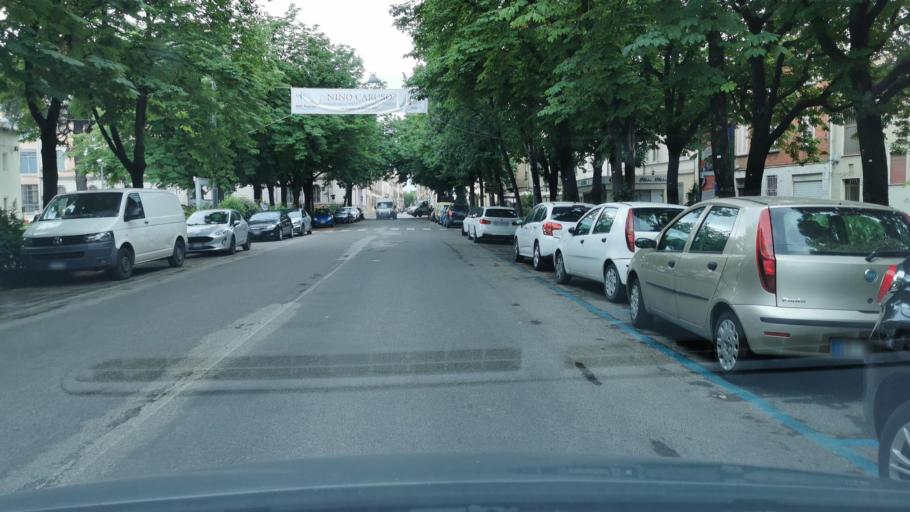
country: IT
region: Emilia-Romagna
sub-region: Provincia di Ravenna
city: Faenza
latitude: 44.2898
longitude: 11.8807
